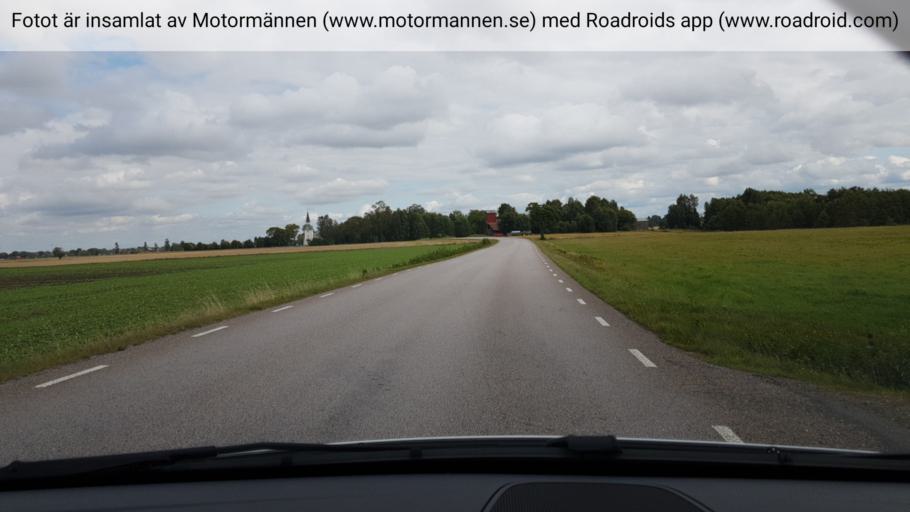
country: SE
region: Vaestra Goetaland
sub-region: Vara Kommun
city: Vara
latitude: 58.2368
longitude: 12.9130
